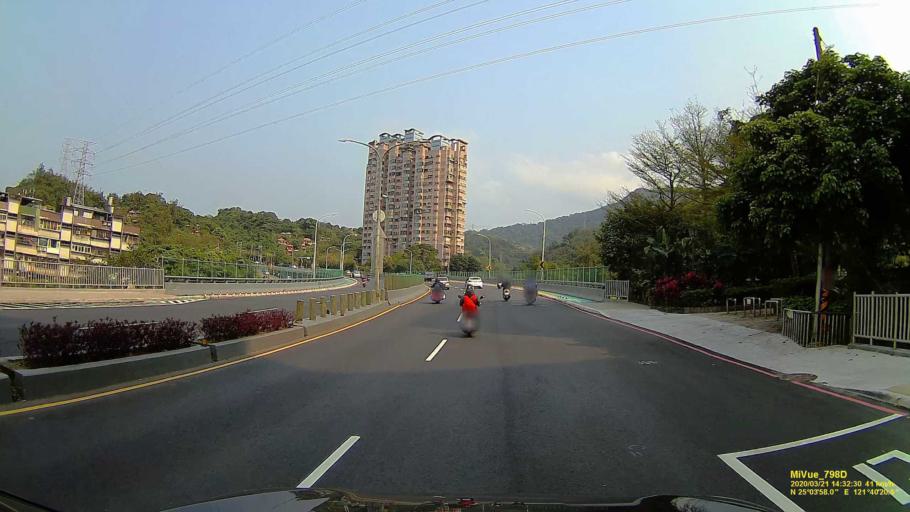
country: TW
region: Taiwan
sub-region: Keelung
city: Keelung
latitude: 25.0659
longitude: 121.6725
